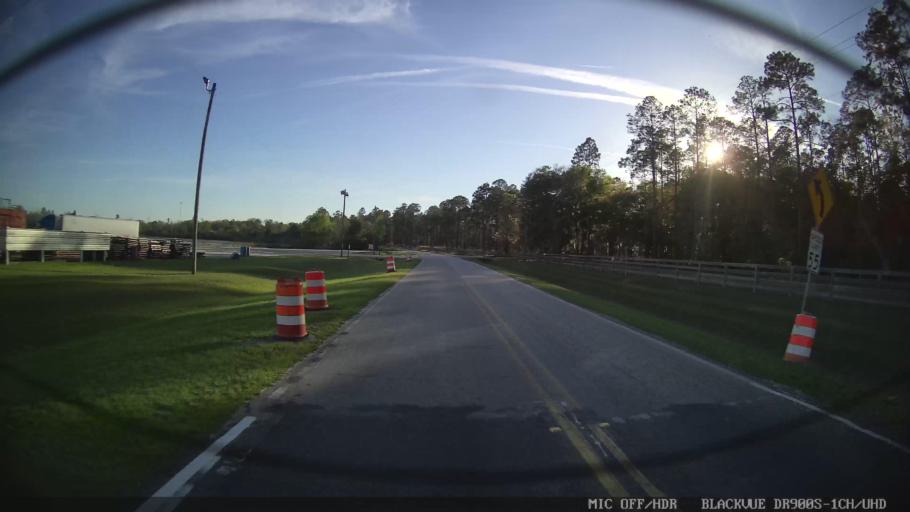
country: US
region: Georgia
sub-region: Echols County
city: Statenville
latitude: 30.6385
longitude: -83.1917
